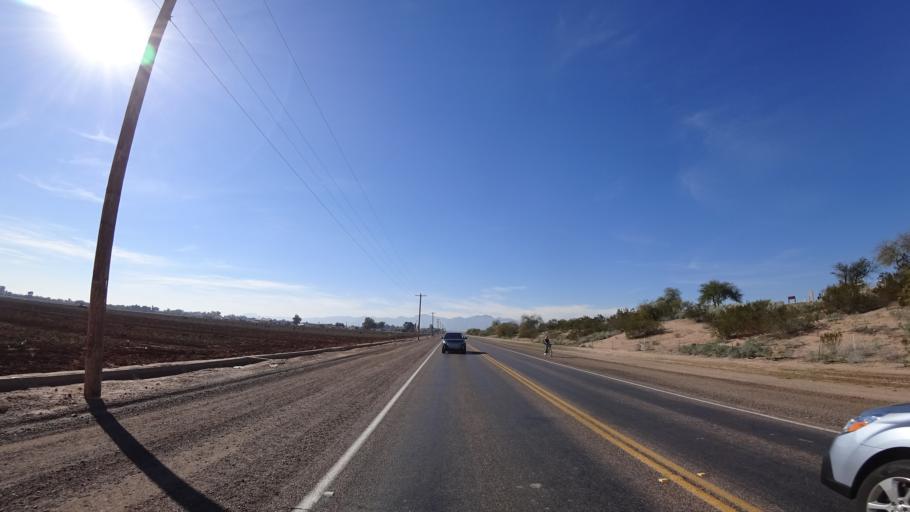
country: US
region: Arizona
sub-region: Maricopa County
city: Citrus Park
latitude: 33.5515
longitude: -112.3865
